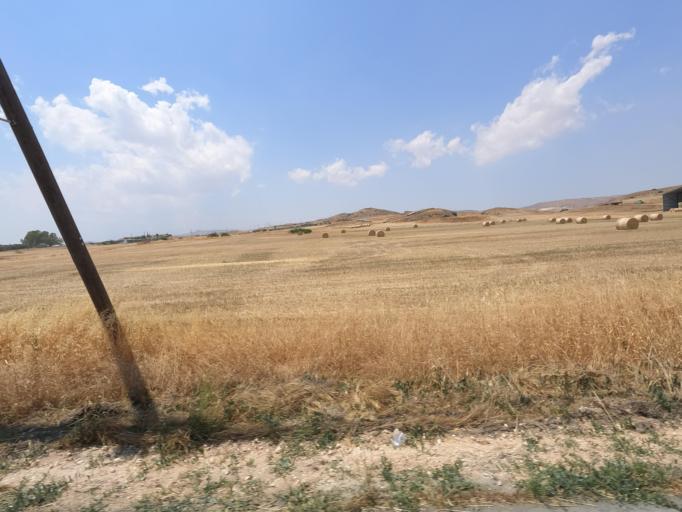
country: CY
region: Larnaka
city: Troulloi
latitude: 35.0191
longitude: 33.6116
